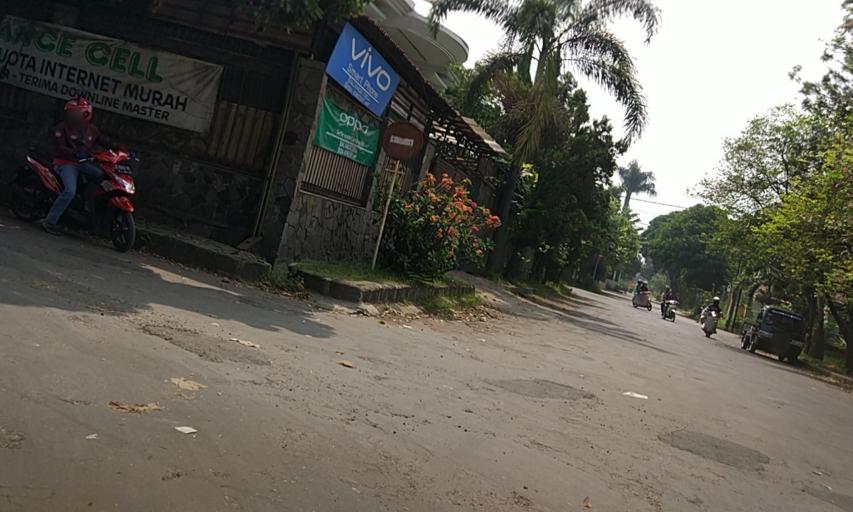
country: ID
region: West Java
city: Margahayukencana
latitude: -6.9479
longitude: 107.5627
